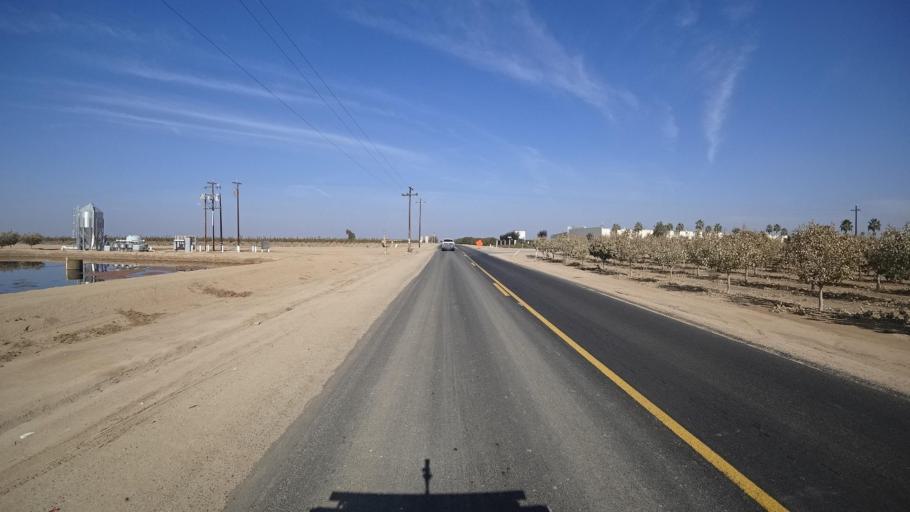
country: US
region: California
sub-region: Kern County
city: Shafter
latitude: 35.5439
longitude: -119.1513
